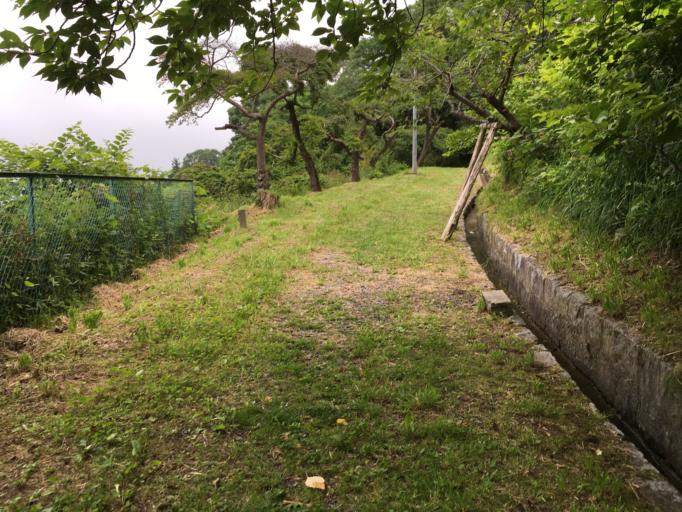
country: JP
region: Iwate
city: Ichinoseki
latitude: 38.9259
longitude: 141.1297
